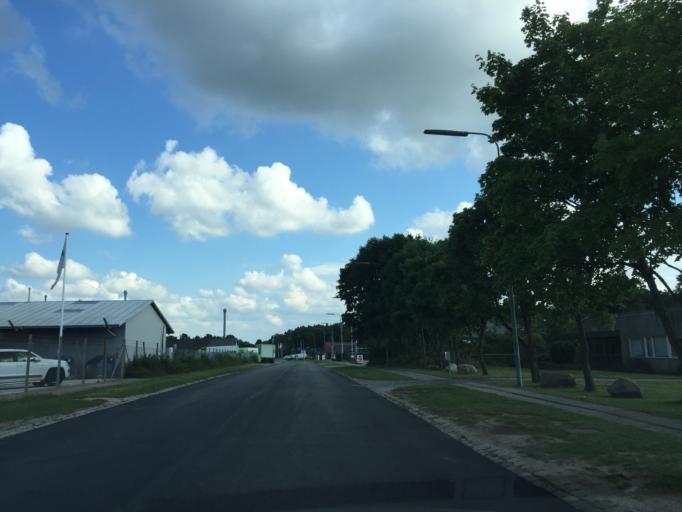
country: DK
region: South Denmark
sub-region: Odense Kommune
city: Neder Holluf
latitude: 55.3858
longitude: 10.4359
